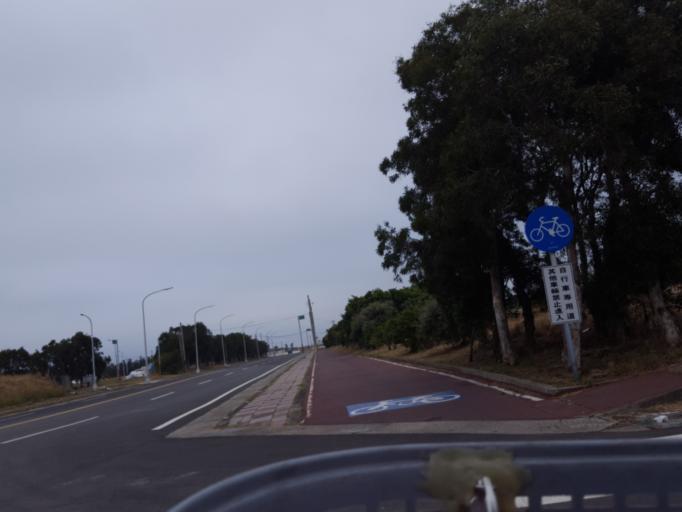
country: TW
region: Taiwan
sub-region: Hsinchu
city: Hsinchu
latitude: 24.7615
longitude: 120.9042
